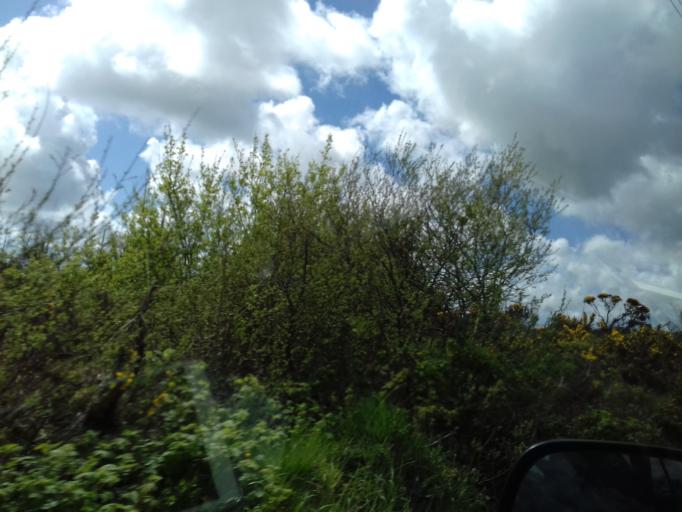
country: IE
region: Leinster
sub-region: Loch Garman
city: Loch Garman
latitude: 52.3145
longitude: -6.5264
